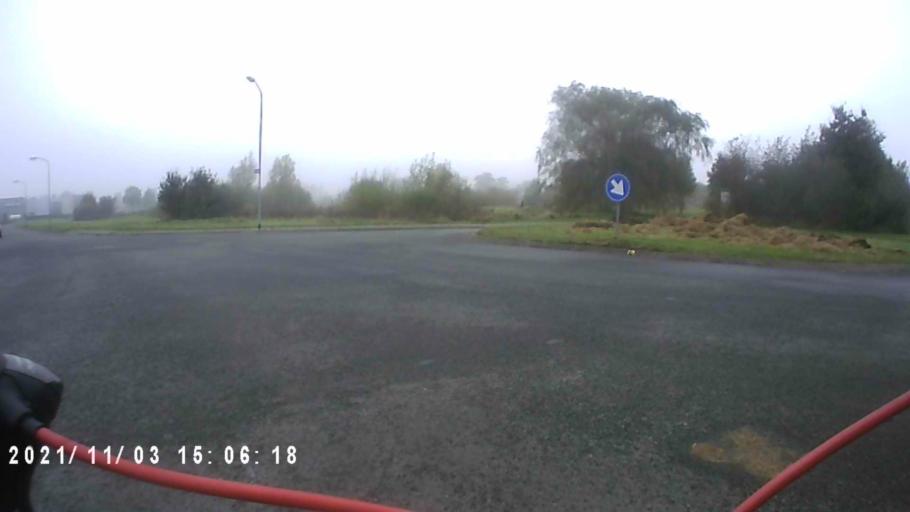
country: NL
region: Groningen
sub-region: Gemeente Leek
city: Leek
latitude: 53.1855
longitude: 6.3705
